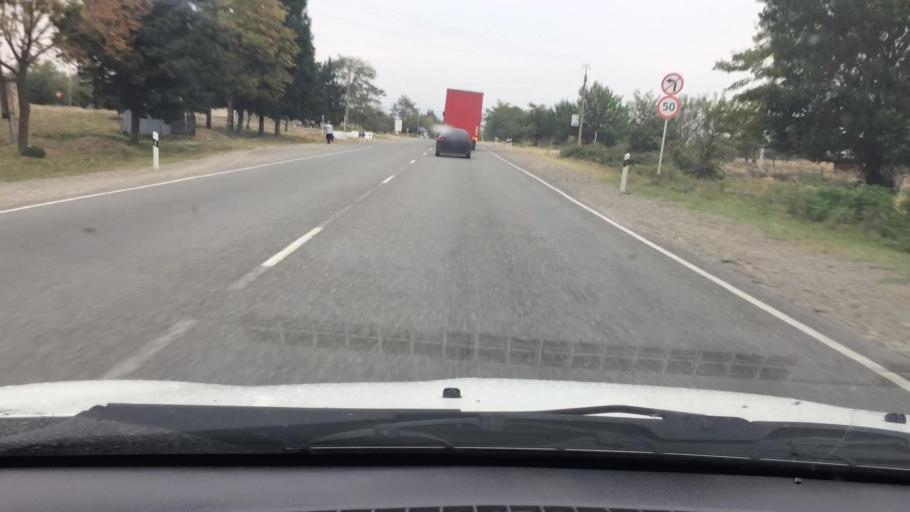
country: GE
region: T'bilisi
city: Tbilisi
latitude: 41.6431
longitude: 44.8537
